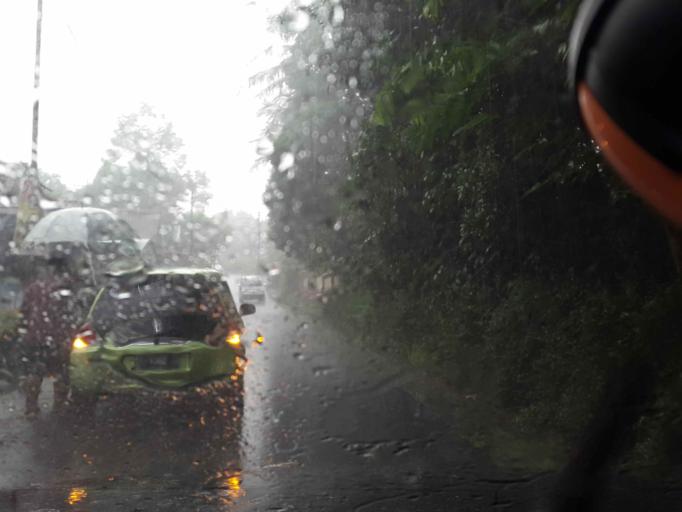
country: ID
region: Central Java
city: Salatiga
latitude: -7.3123
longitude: 110.4895
